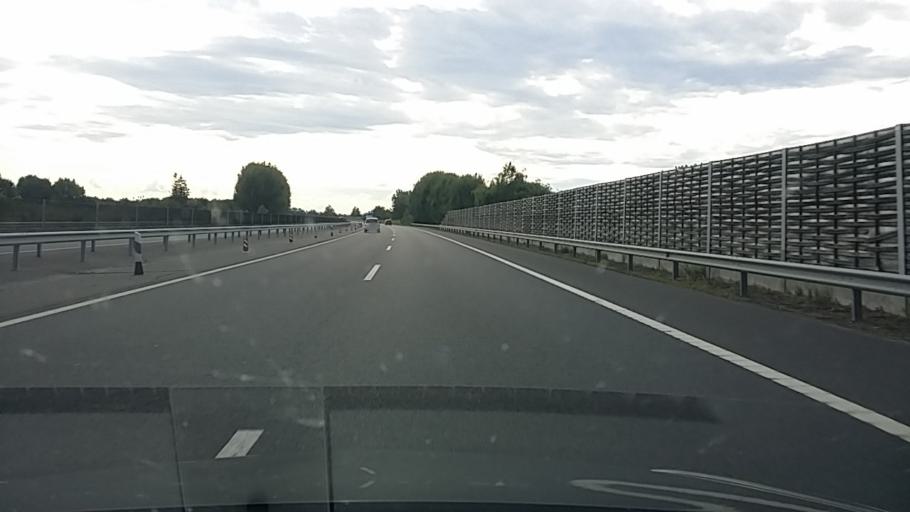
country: HU
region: Szabolcs-Szatmar-Bereg
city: Nyiregyhaza
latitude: 47.9016
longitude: 21.6667
